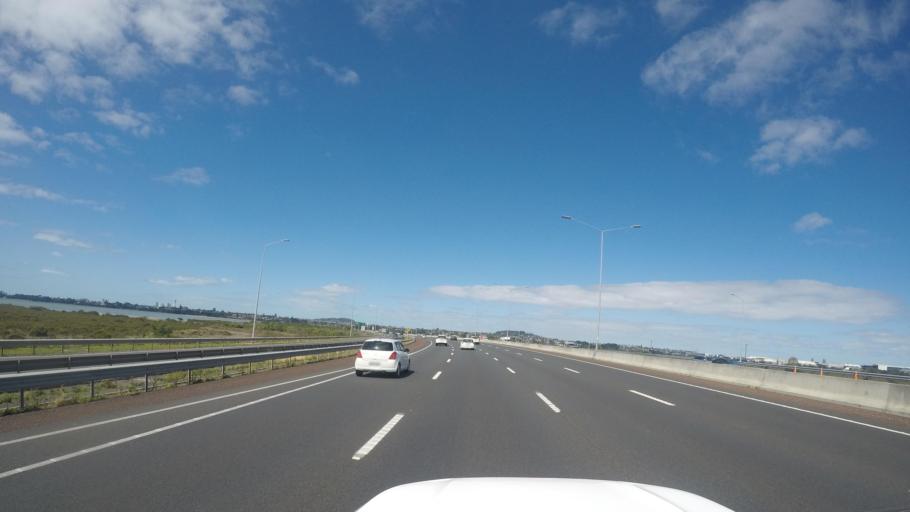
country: NZ
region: Auckland
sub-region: Auckland
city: Rosebank
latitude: -36.8705
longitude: 174.6770
